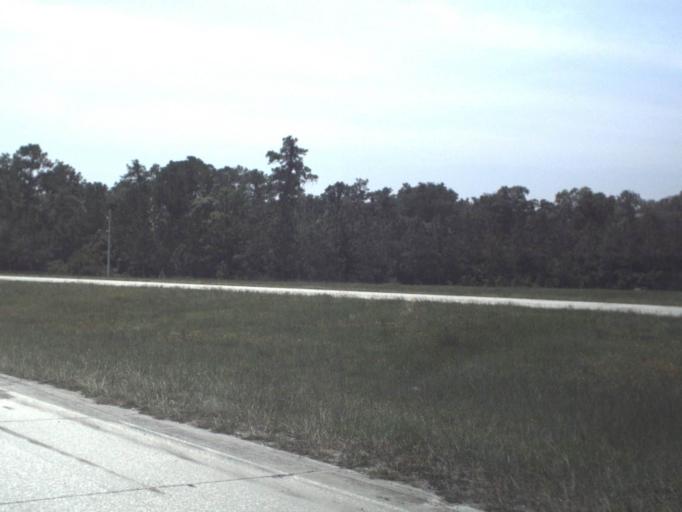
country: US
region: Florida
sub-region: Saint Johns County
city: Fruit Cove
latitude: 30.1659
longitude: -81.5553
